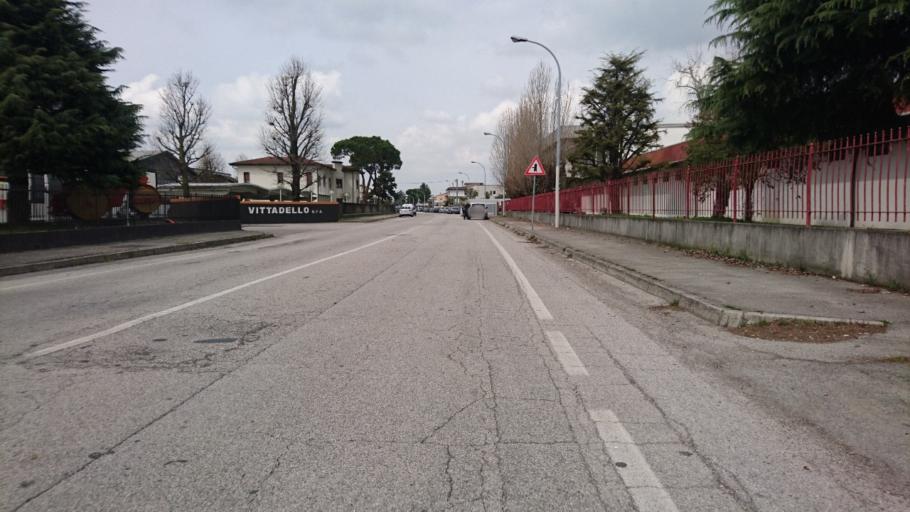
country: IT
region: Veneto
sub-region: Provincia di Padova
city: Saletto
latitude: 45.4595
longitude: 11.8590
